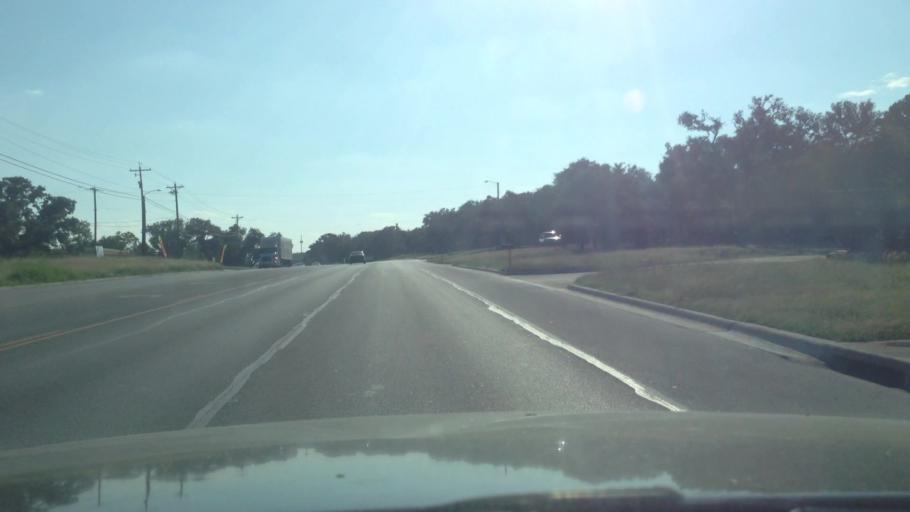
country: US
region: Texas
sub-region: Hays County
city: San Marcos
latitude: 29.8518
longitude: -97.9743
